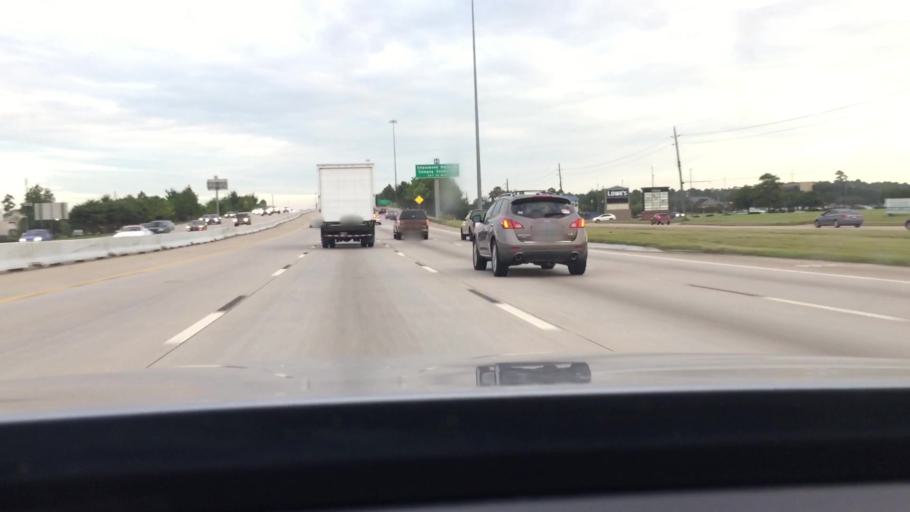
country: US
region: Texas
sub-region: Harris County
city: Oak Cliff Place
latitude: 29.9773
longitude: -95.5653
